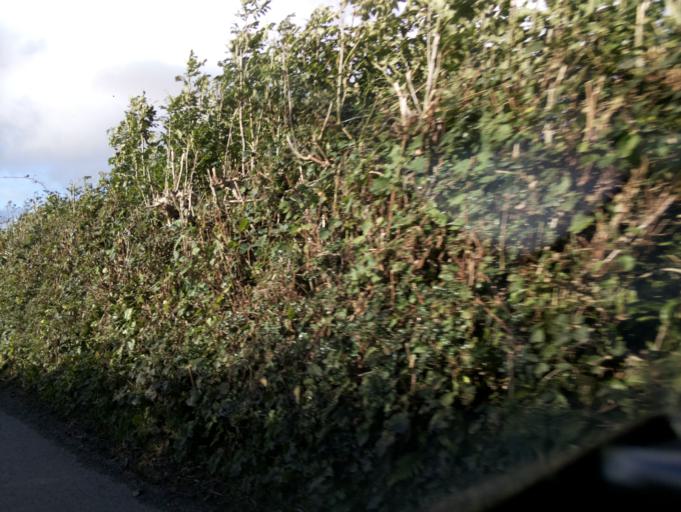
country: GB
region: England
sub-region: Devon
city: Totnes
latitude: 50.3563
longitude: -3.7275
